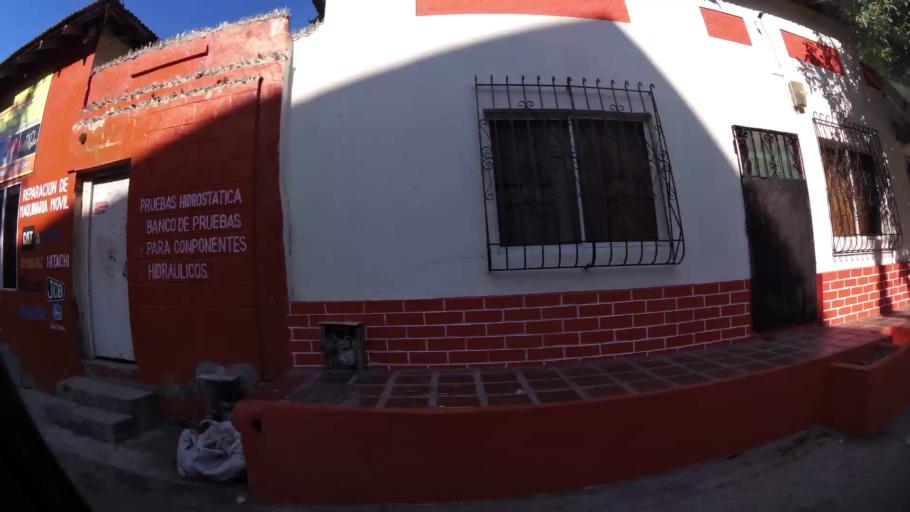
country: CO
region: Atlantico
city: Barranquilla
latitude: 10.9909
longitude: -74.7824
